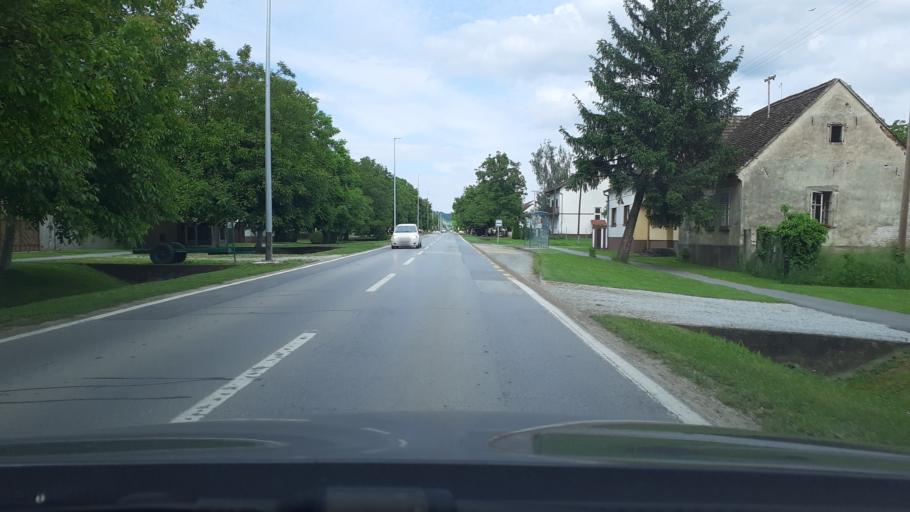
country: HR
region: Brodsko-Posavska
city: Sibinj
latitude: 45.1801
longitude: 17.8793
